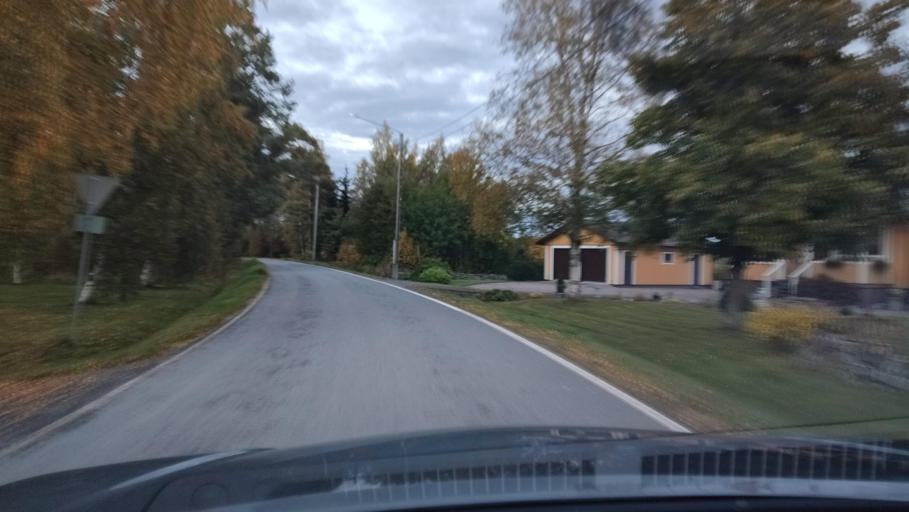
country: FI
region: Ostrobothnia
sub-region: Sydosterbotten
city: Kristinestad
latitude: 62.2622
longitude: 21.5087
